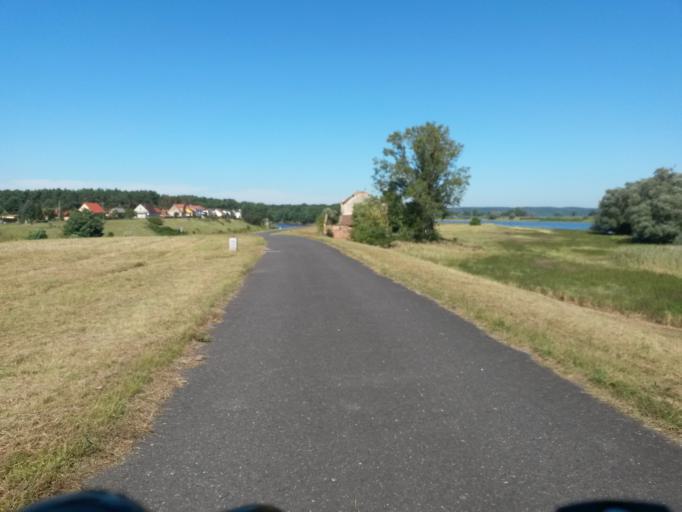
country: PL
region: West Pomeranian Voivodeship
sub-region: Powiat gryfinski
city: Cedynia
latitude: 52.8816
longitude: 14.1561
